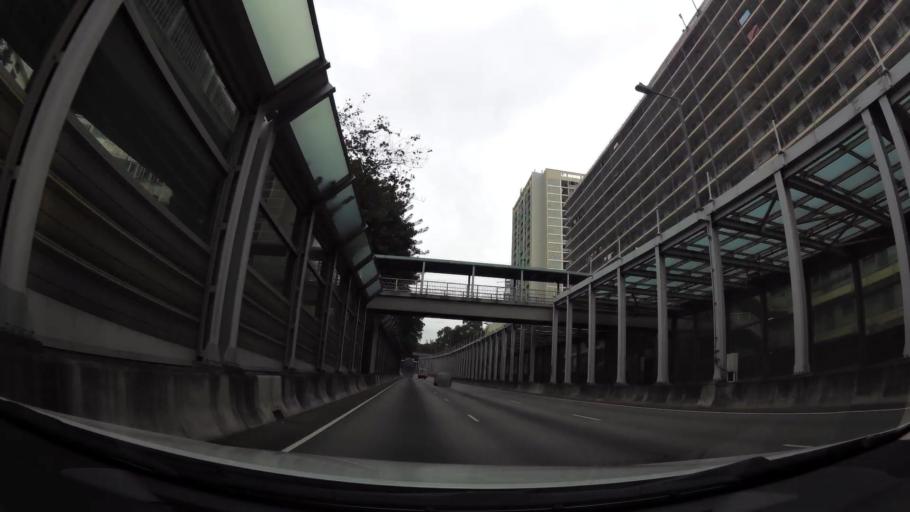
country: HK
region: Tsuen Wan
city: Tsuen Wan
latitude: 22.3789
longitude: 114.1295
